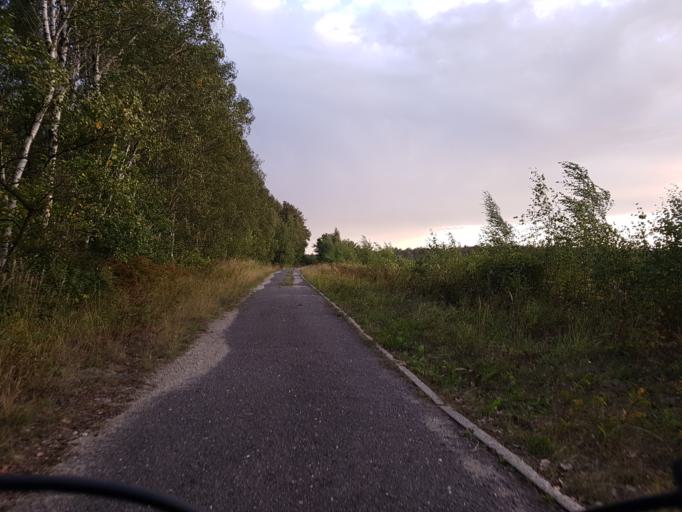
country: DE
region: Brandenburg
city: Trobitz
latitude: 51.5824
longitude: 13.4436
